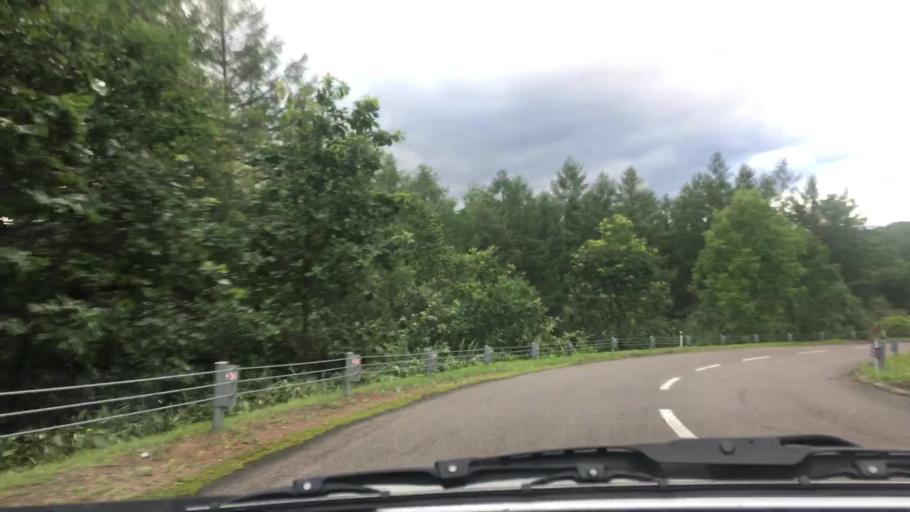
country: JP
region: Hokkaido
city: Otofuke
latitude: 43.1530
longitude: 142.8586
